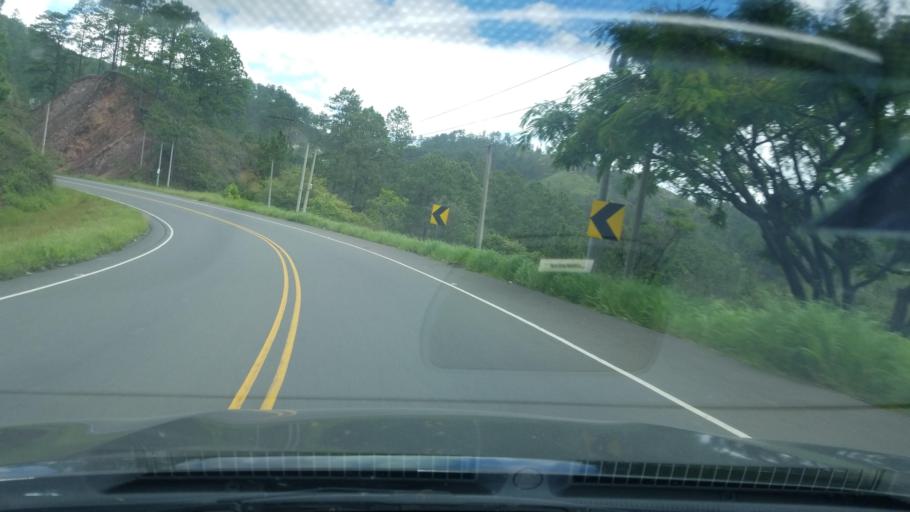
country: HN
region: Francisco Morazan
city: Talanga
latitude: 14.3652
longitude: -87.1423
